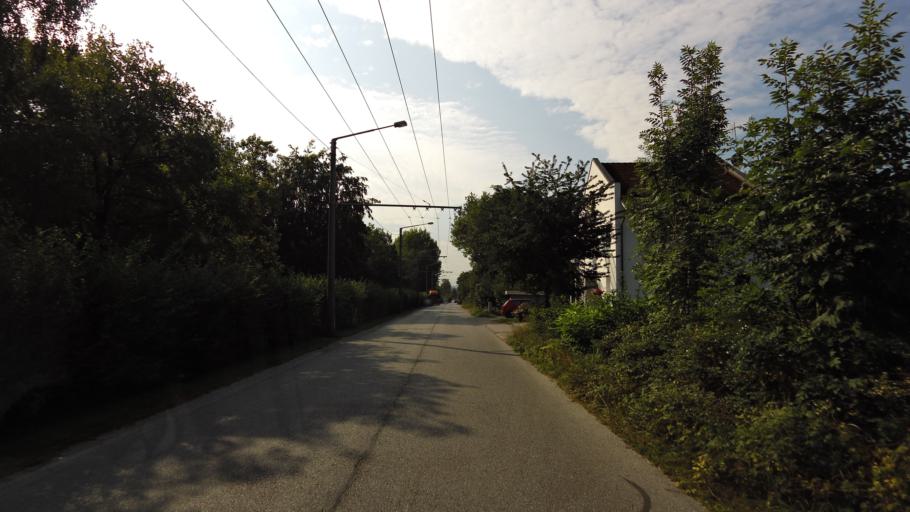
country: AT
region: Salzburg
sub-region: Politischer Bezirk Salzburg-Umgebung
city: Bergheim
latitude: 47.8346
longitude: 13.0171
